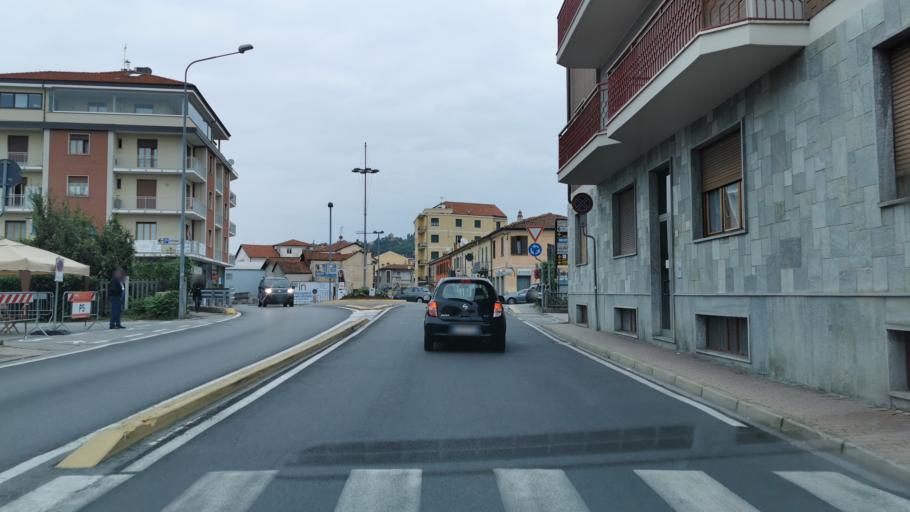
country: IT
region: Piedmont
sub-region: Provincia di Cuneo
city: Bra
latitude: 44.6919
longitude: 7.8549
